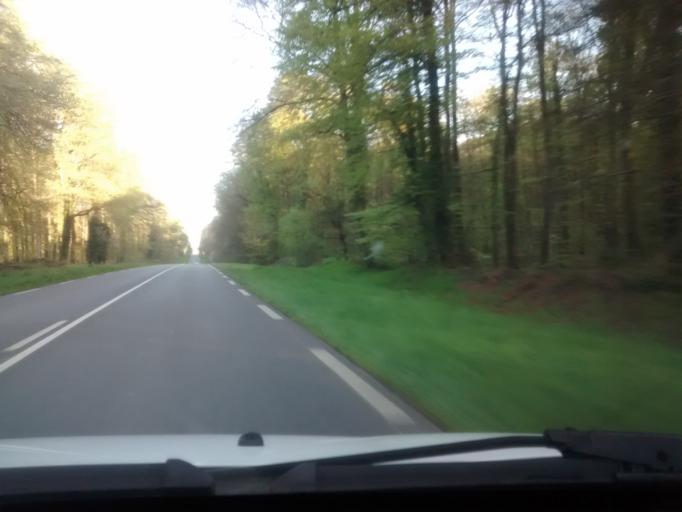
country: FR
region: Brittany
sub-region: Departement d'Ille-et-Vilaine
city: Pleine-Fougeres
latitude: 48.4826
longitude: -1.5598
